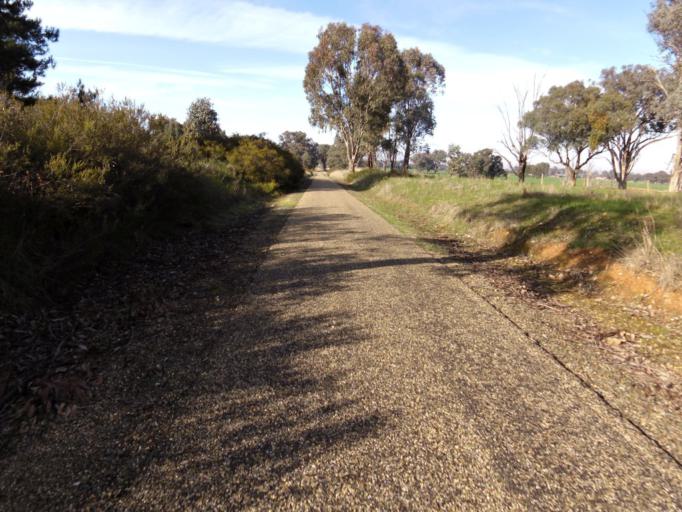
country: AU
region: Victoria
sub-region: Wangaratta
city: Wangaratta
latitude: -36.4189
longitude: 146.5501
